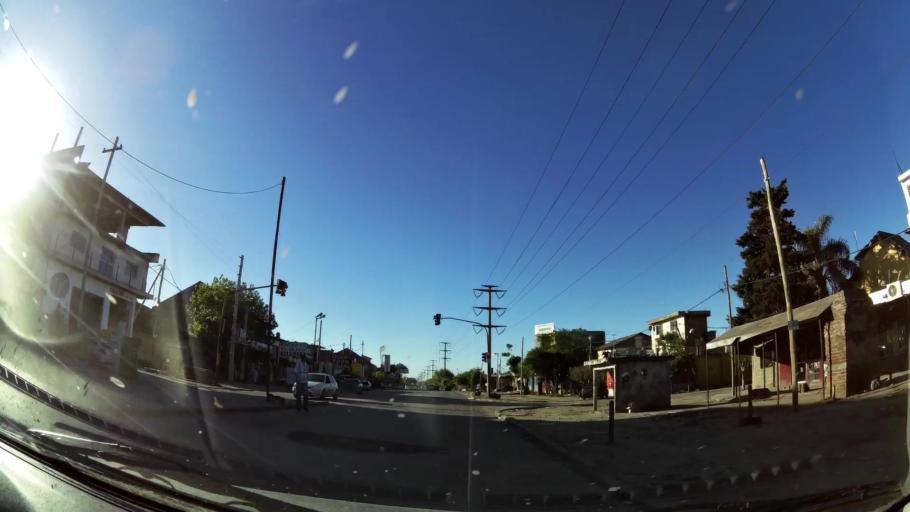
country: AR
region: Buenos Aires
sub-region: Partido de Almirante Brown
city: Adrogue
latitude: -34.7687
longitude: -58.3260
